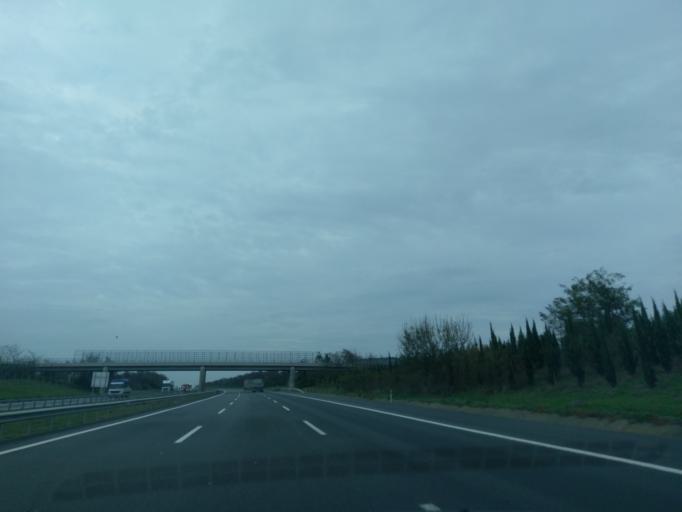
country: TR
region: Istanbul
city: Canta
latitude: 41.1597
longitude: 28.1373
